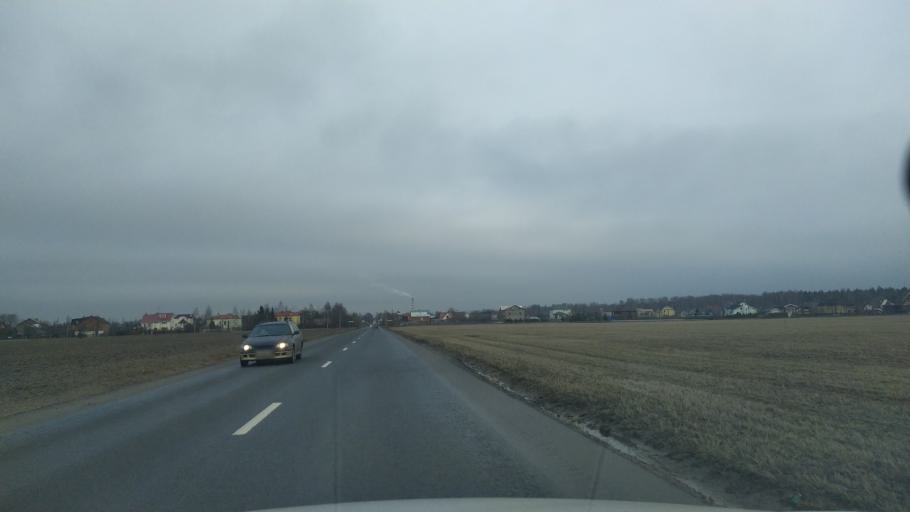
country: RU
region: St.-Petersburg
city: Aleksandrovskaya
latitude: 59.7197
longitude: 30.3424
